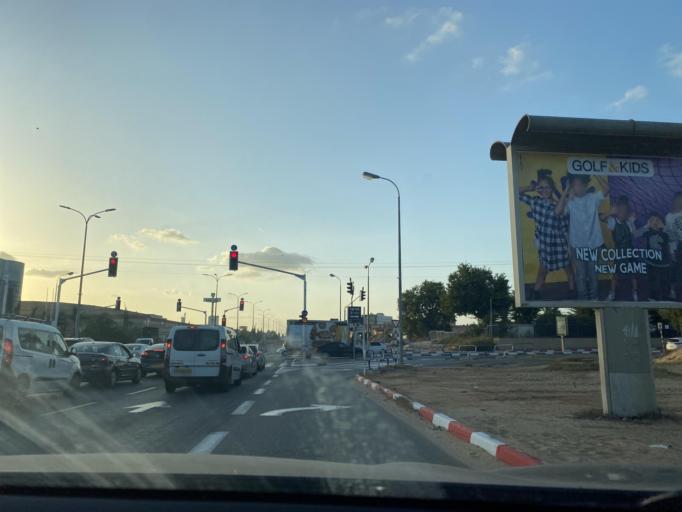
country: IL
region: Southern District
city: Ashdod
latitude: 31.8094
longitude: 34.6596
